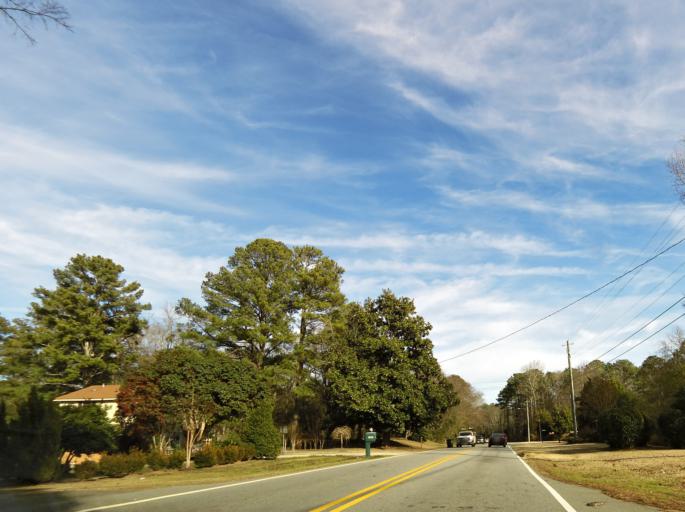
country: US
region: Georgia
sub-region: Bibb County
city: West Point
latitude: 32.8631
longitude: -83.7377
